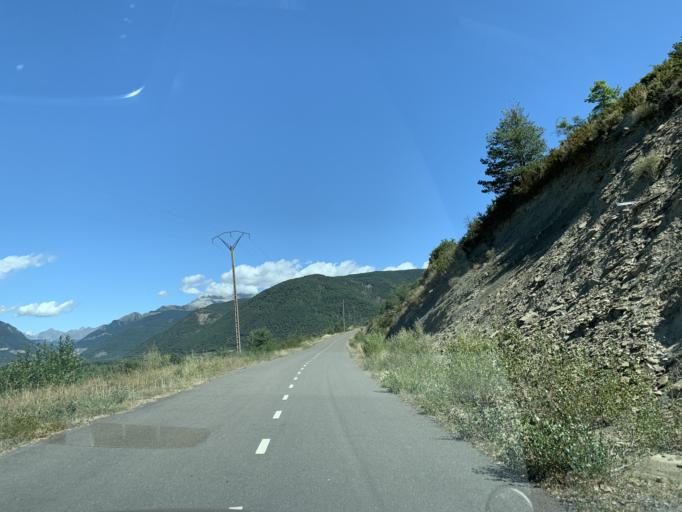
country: ES
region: Aragon
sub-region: Provincia de Huesca
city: Sabinanigo
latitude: 42.5565
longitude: -0.3173
